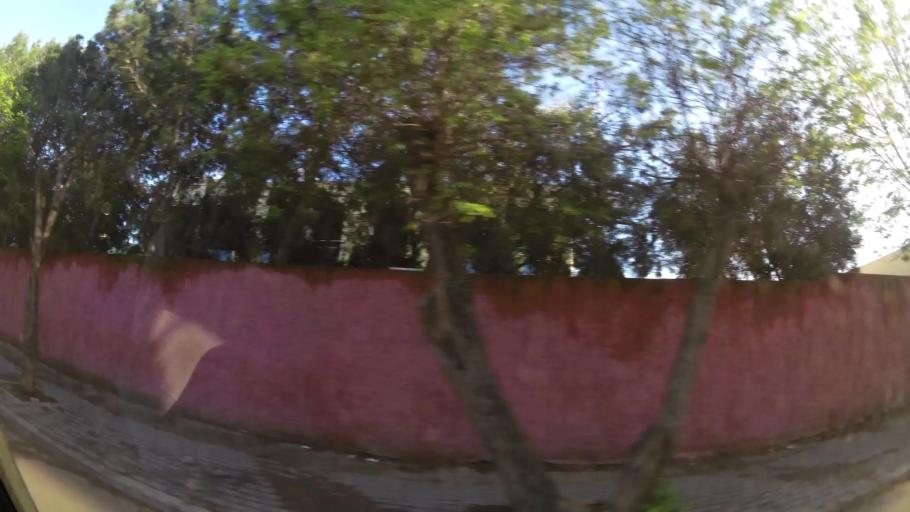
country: MA
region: Chaouia-Ouardigha
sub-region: Settat Province
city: Settat
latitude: 33.0007
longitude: -7.6121
